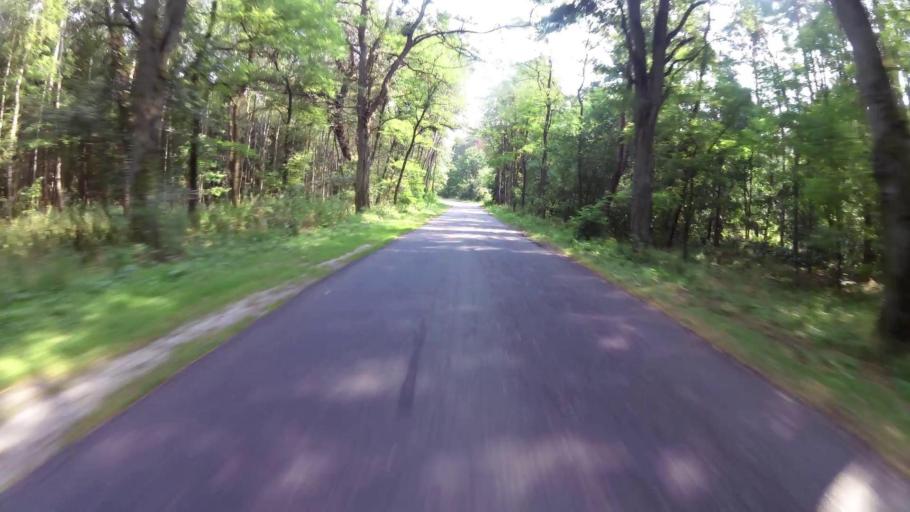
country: PL
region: West Pomeranian Voivodeship
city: Trzcinsko Zdroj
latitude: 52.8577
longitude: 14.6442
